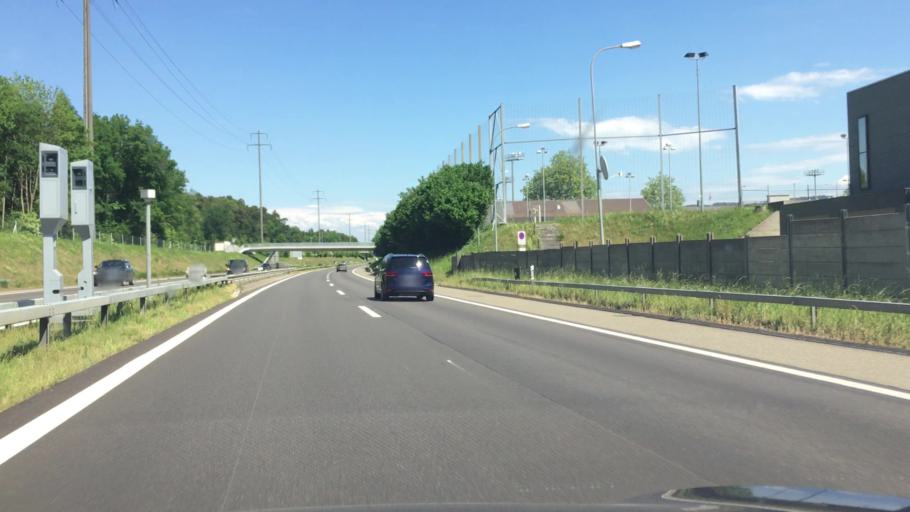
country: CH
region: Thurgau
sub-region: Frauenfeld District
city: Frauenfeld
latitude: 47.5650
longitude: 8.8837
